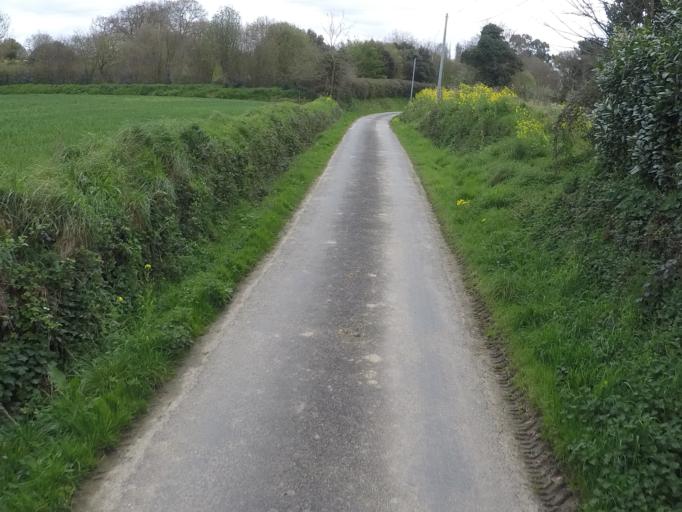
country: FR
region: Brittany
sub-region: Departement des Cotes-d'Armor
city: Plouha
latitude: 48.6584
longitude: -2.9177
